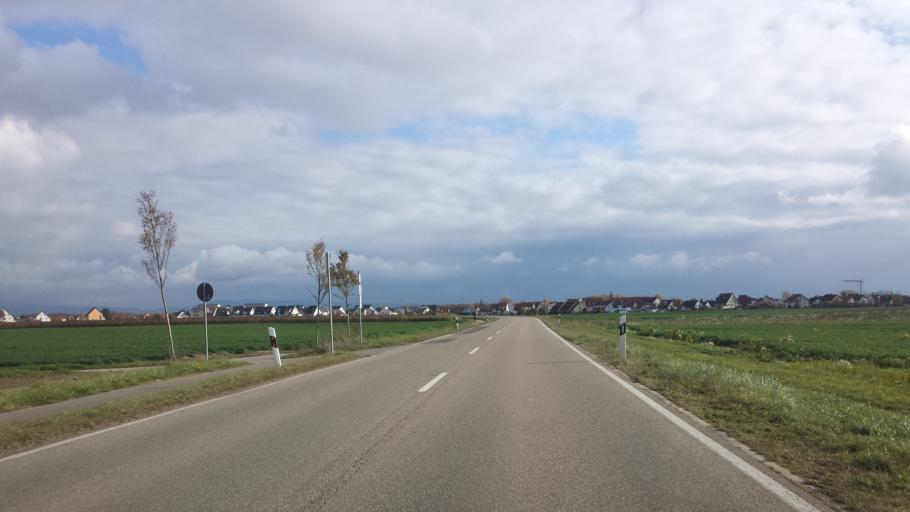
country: DE
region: Rheinland-Pfalz
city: Waldsee
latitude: 49.4009
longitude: 8.4244
